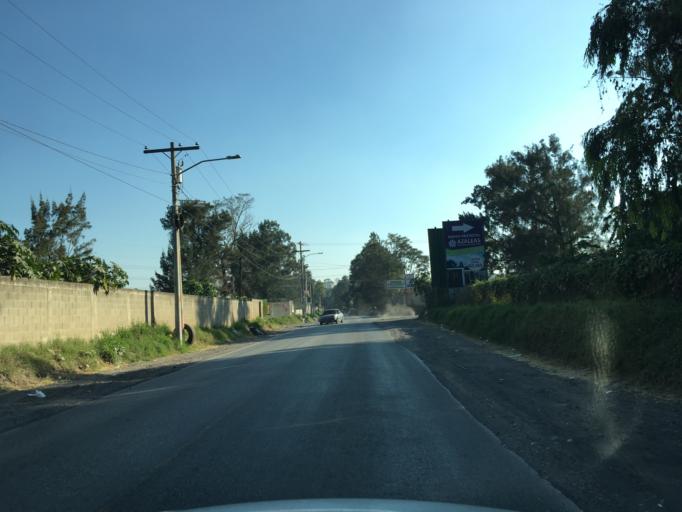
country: GT
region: Guatemala
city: Villa Nueva
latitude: 14.5278
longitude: -90.6169
